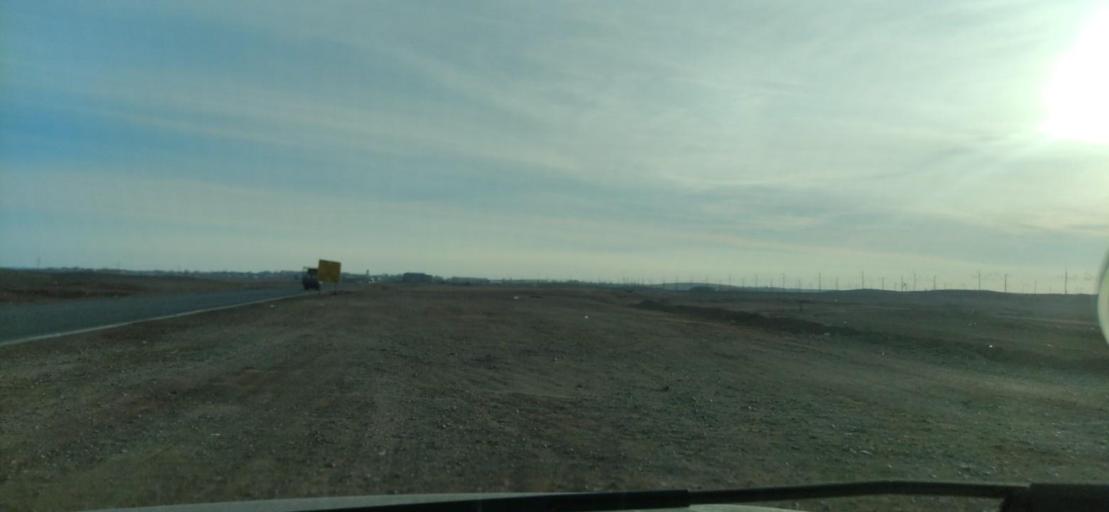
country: KZ
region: Qaraghandy
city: Saryshaghan
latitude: 46.1457
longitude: 73.6083
